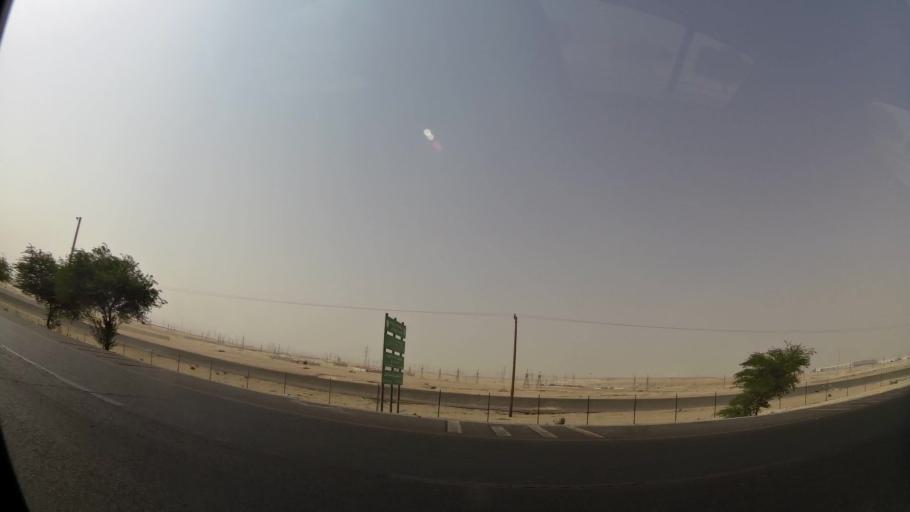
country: KW
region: Muhafazat al Jahra'
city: Al Jahra'
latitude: 29.3286
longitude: 47.6344
